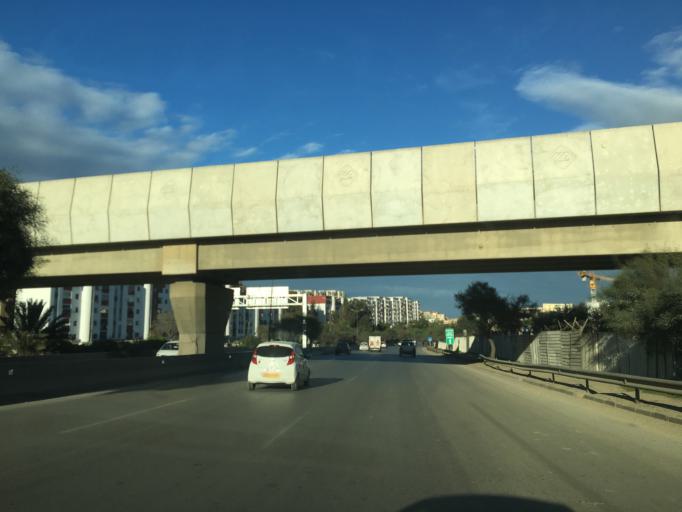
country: DZ
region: Tipaza
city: Baraki
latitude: 36.7198
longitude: 3.1044
